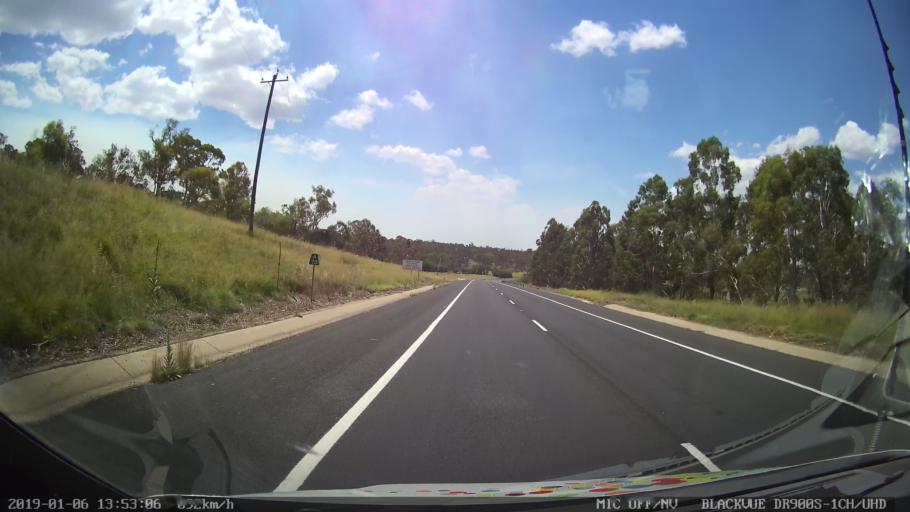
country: AU
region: New South Wales
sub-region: Tamworth Municipality
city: Kootingal
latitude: -30.9123
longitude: 151.1360
